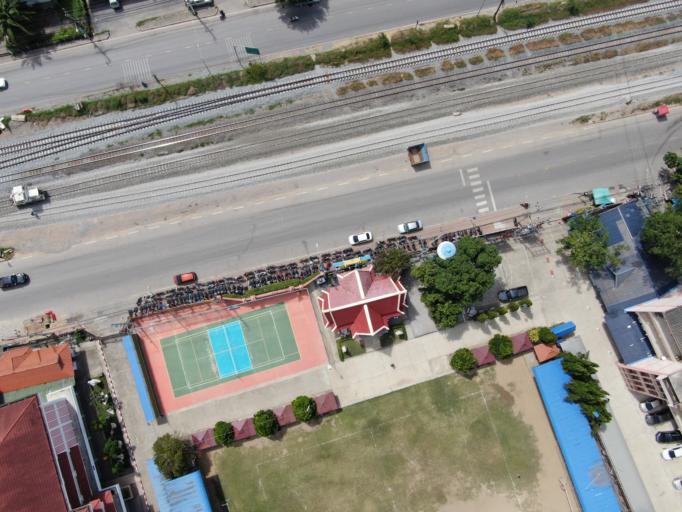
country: TH
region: Ratchaburi
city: Ban Pong
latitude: 13.8061
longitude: 99.8737
